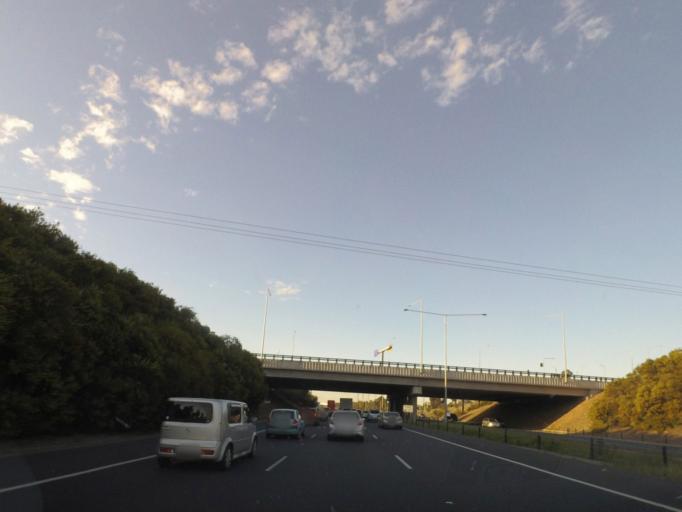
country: AU
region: Victoria
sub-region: Monash
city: Mulgrave
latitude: -37.9262
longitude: 145.2126
